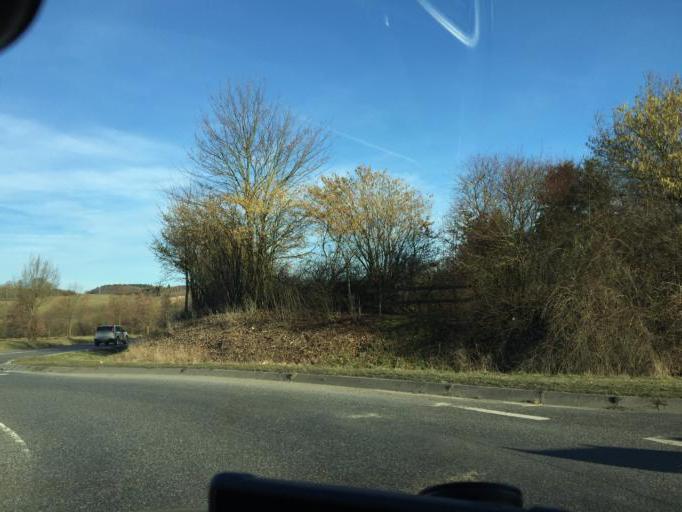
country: DE
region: Rheinland-Pfalz
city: Niederahr
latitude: 50.4756
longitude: 7.8600
